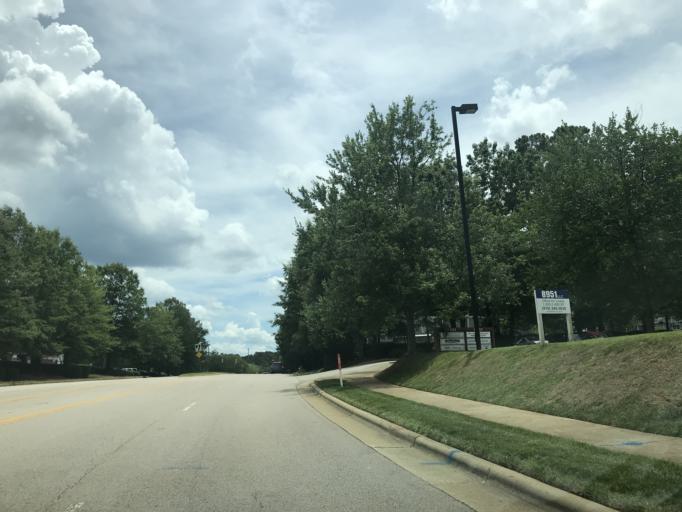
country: US
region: North Carolina
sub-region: Wake County
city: West Raleigh
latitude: 35.9063
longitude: -78.6581
